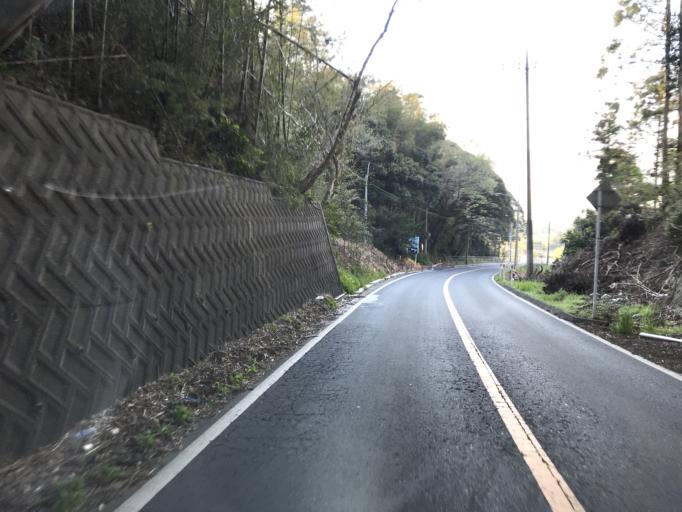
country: JP
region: Chiba
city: Yokaichiba
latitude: 35.7283
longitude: 140.5610
